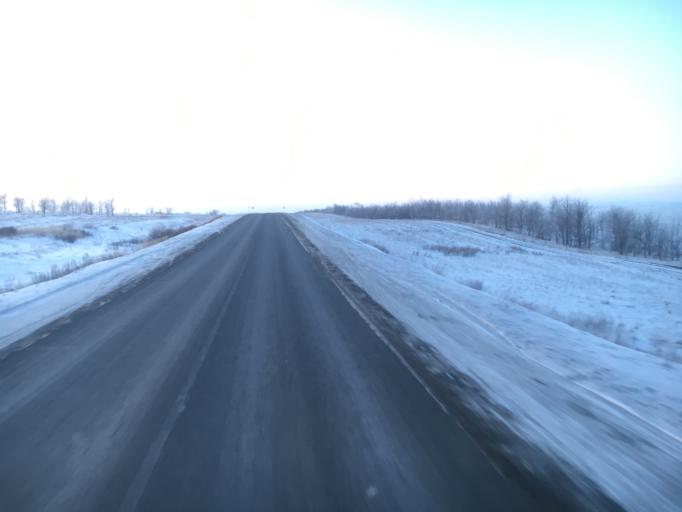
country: KZ
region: Aqtoebe
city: Aqtobe
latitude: 50.2843
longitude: 57.7336
